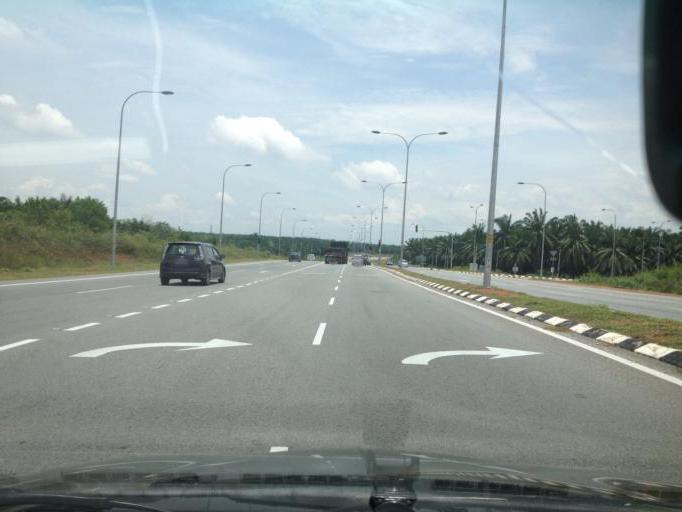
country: MY
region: Kedah
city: Sungai Petani
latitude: 5.6115
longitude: 100.5673
